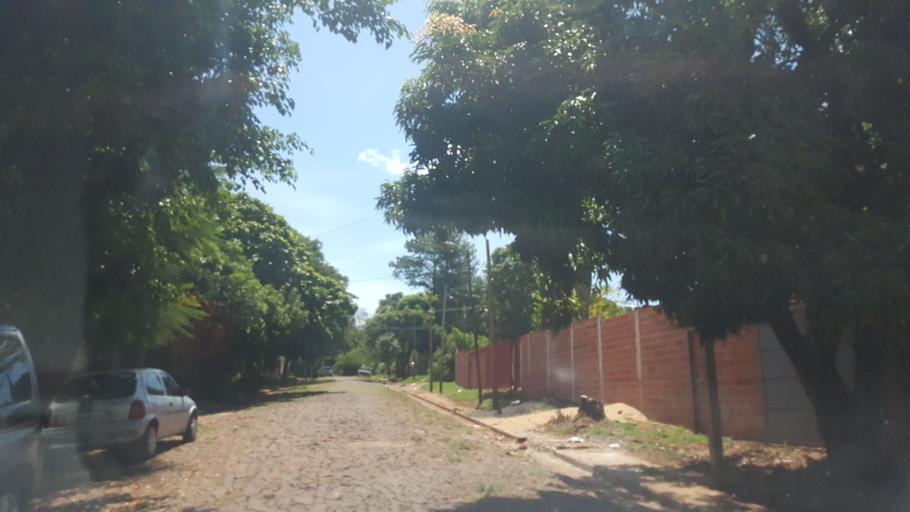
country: AR
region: Misiones
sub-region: Departamento de Capital
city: Posadas
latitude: -27.3706
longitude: -55.9189
